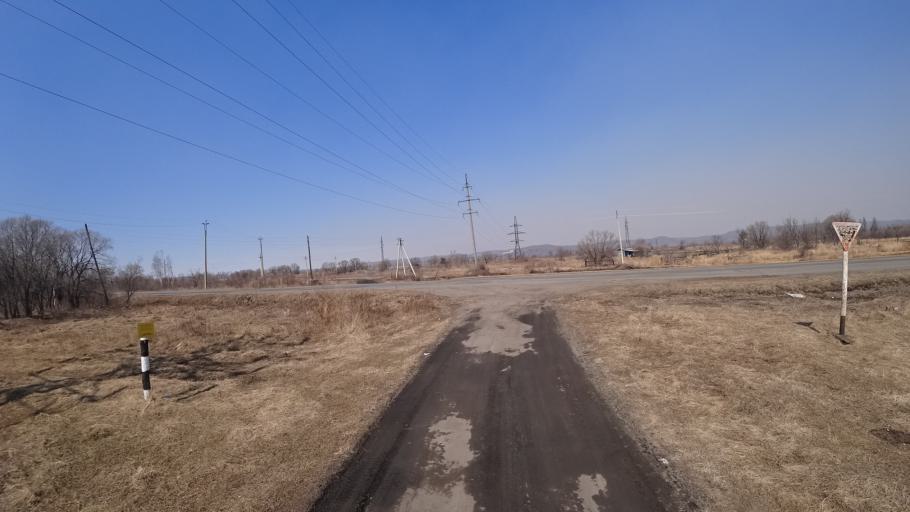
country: RU
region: Amur
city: Bureya
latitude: 49.7897
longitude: 129.8393
